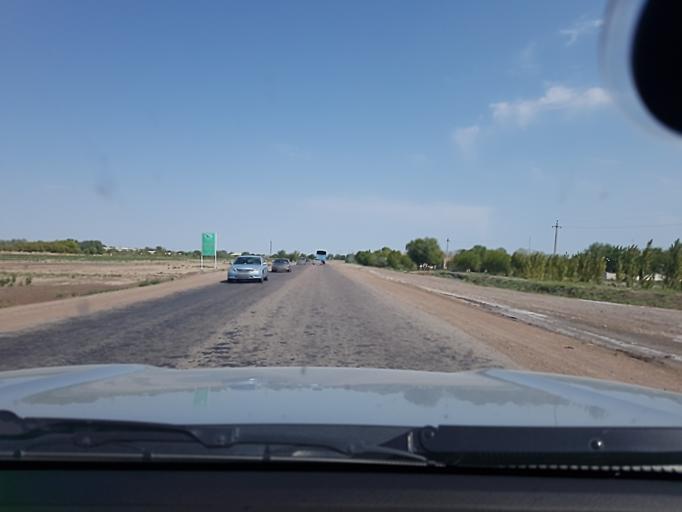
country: TM
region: Dasoguz
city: Boldumsaz
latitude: 42.1580
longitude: 59.6067
